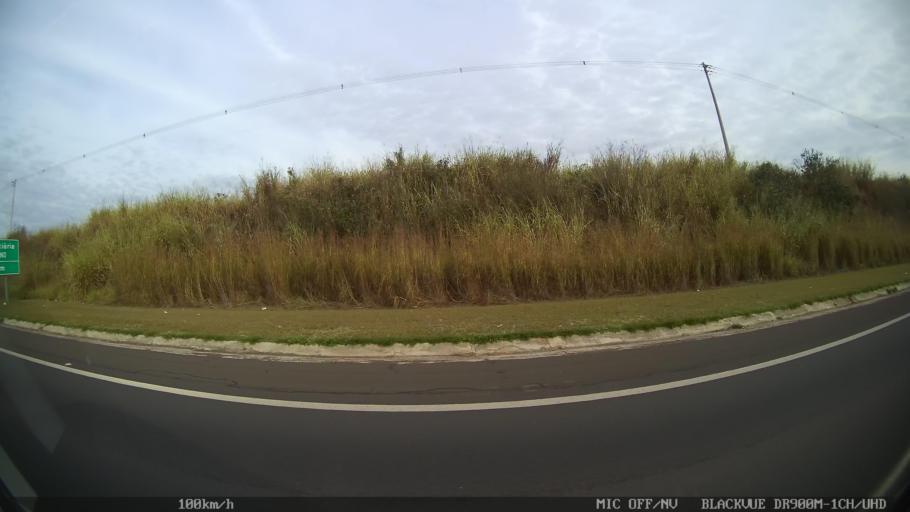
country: BR
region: Sao Paulo
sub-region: Piracicaba
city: Piracicaba
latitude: -22.6825
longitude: -47.5756
